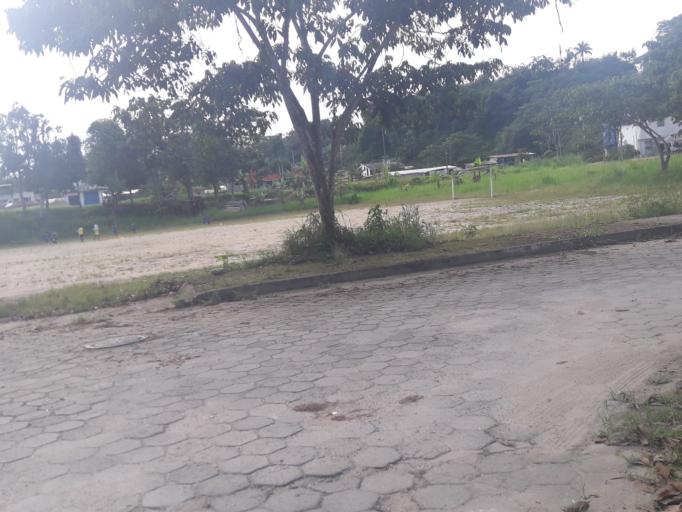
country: EC
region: Napo
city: Tena
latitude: -0.9890
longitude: -77.8089
